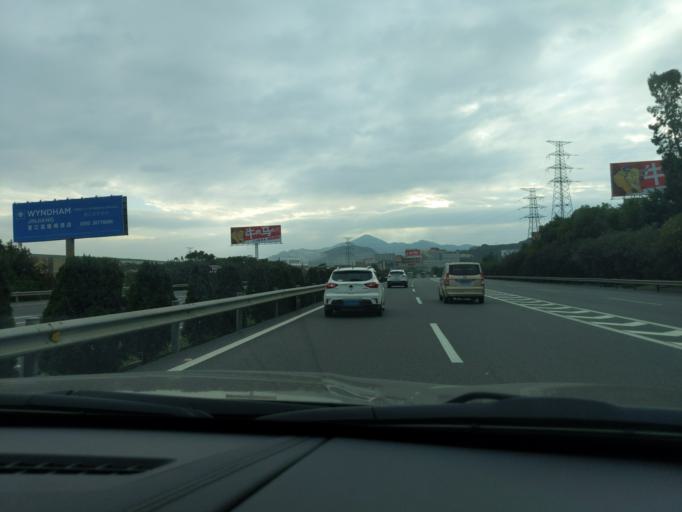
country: CN
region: Fujian
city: Dongshi
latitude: 24.7081
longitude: 118.3909
